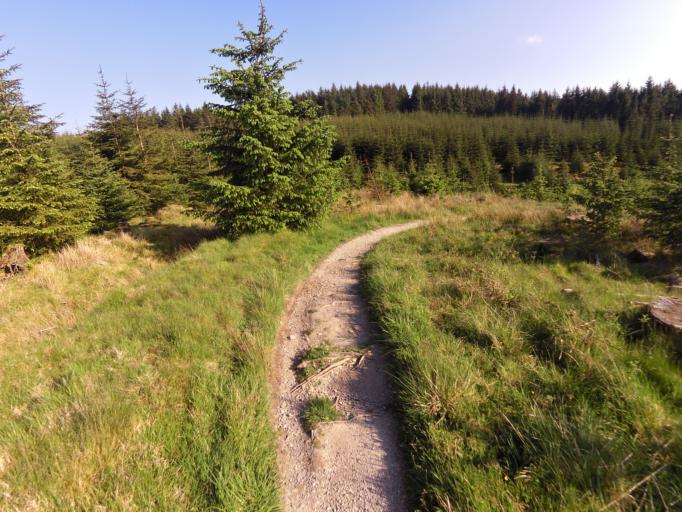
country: GB
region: England
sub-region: North Yorkshire
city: Settle
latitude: 54.0215
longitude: -2.3849
